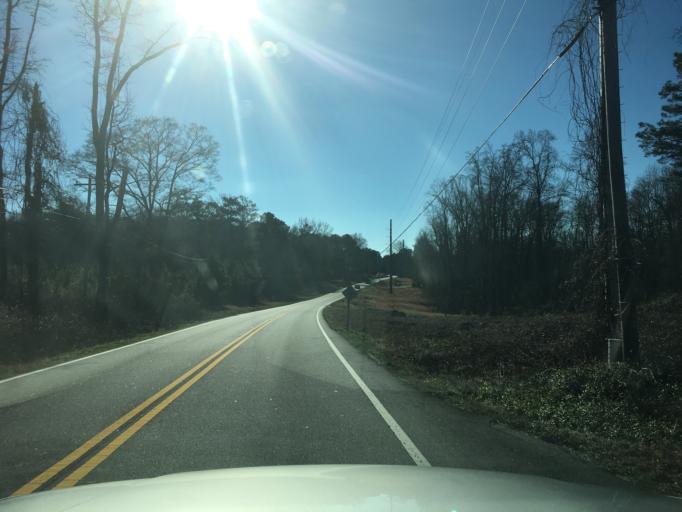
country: US
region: Georgia
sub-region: Carroll County
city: Villa Rica
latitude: 33.7156
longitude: -84.8355
